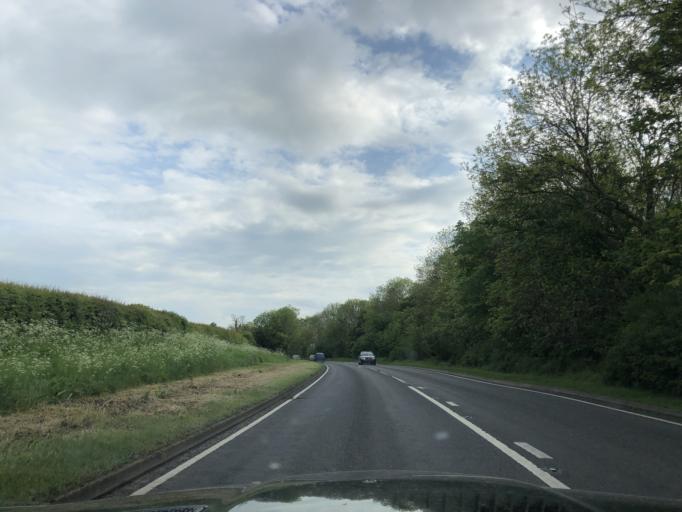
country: GB
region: England
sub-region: Warwickshire
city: Shipston on Stour
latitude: 52.1257
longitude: -1.6185
